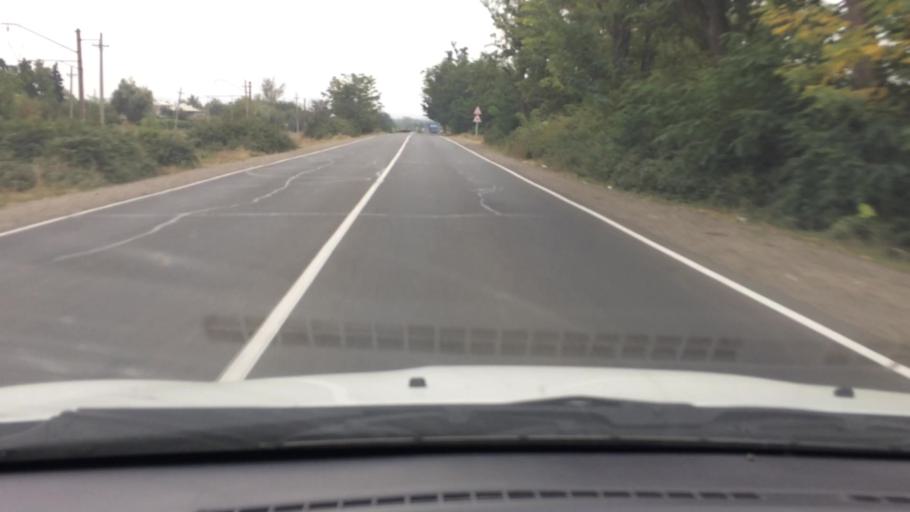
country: GE
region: Kvemo Kartli
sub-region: Marneuli
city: Marneuli
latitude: 41.4144
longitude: 44.8279
